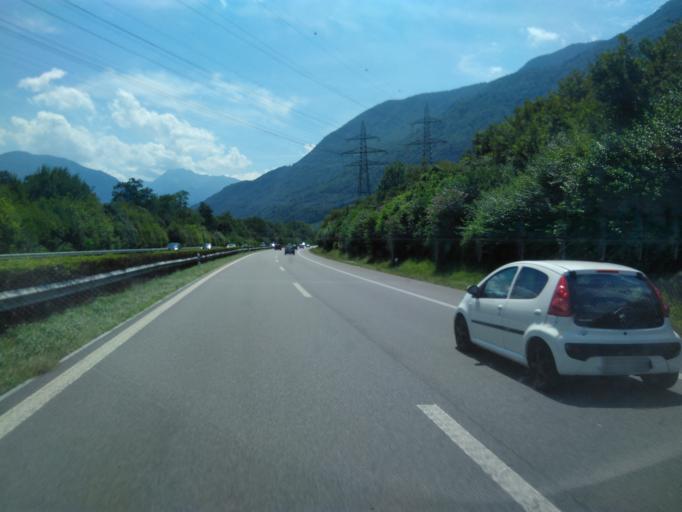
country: CH
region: Ticino
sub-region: Riviera District
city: Claro
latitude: 46.2620
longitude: 9.0094
